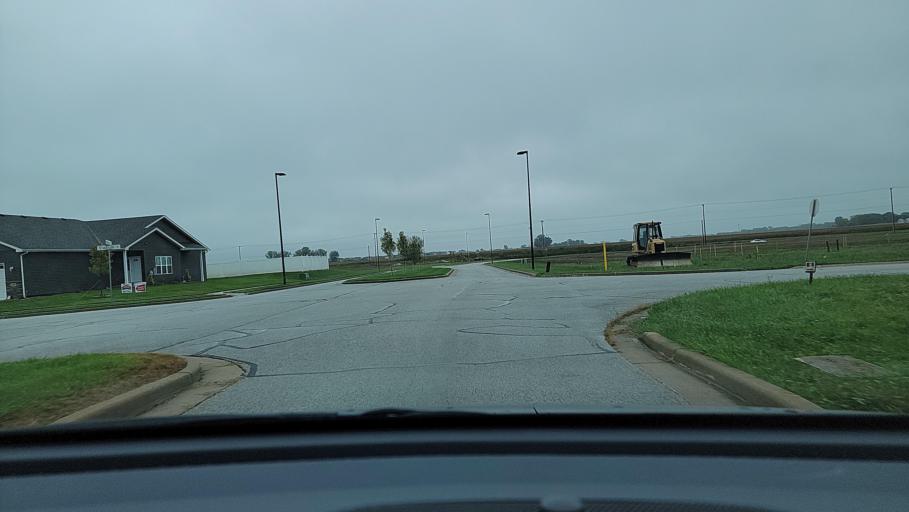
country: US
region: Indiana
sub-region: Porter County
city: Portage
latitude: 41.5389
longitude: -87.1849
